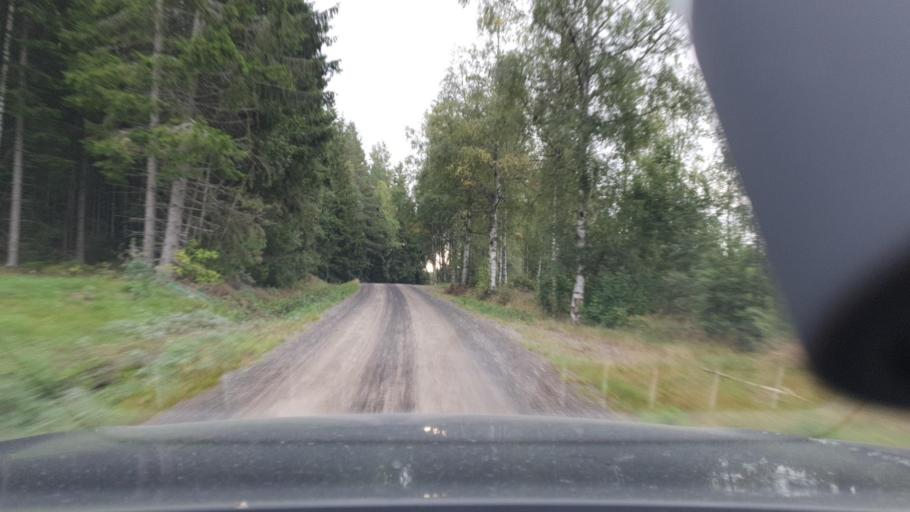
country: SE
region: Vaermland
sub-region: Arvika Kommun
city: Arvika
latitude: 59.8639
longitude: 12.8237
